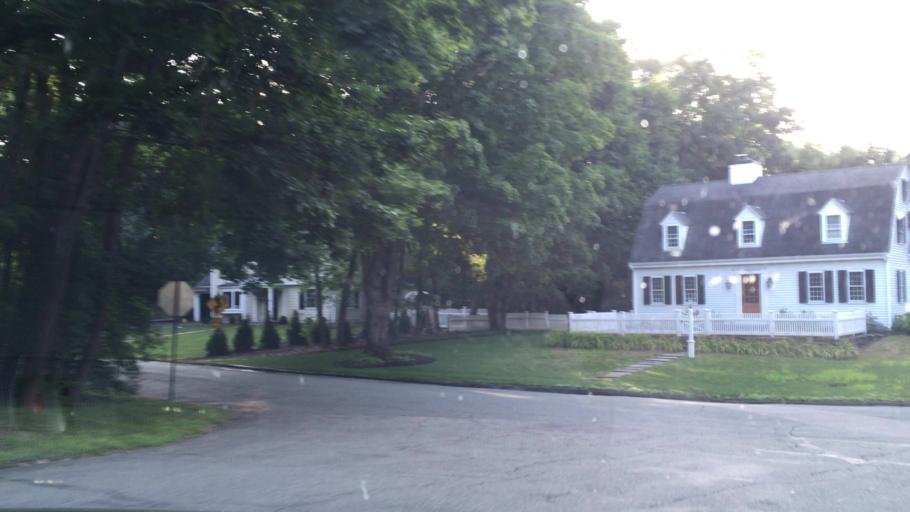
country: US
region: Massachusetts
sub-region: Norfolk County
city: Wellesley
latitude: 42.3100
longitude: -71.2850
